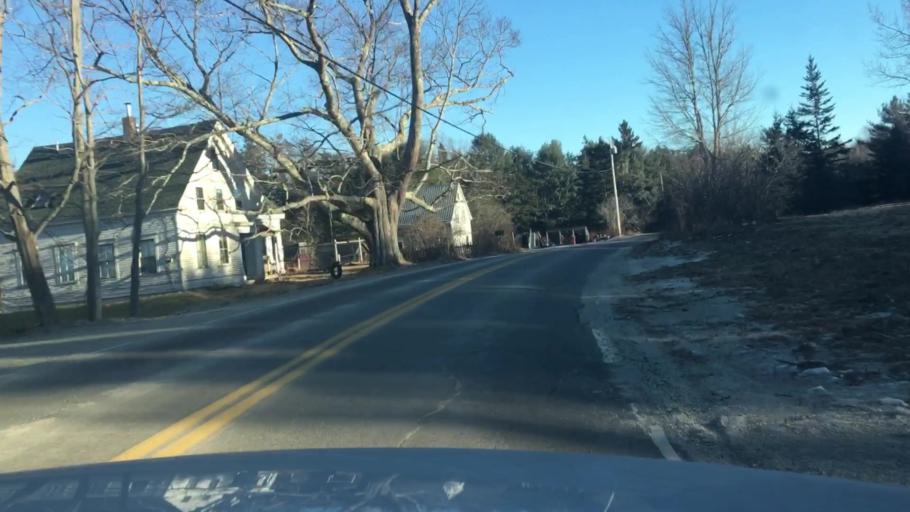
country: US
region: Maine
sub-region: Hancock County
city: Penobscot
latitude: 44.3890
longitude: -68.6993
